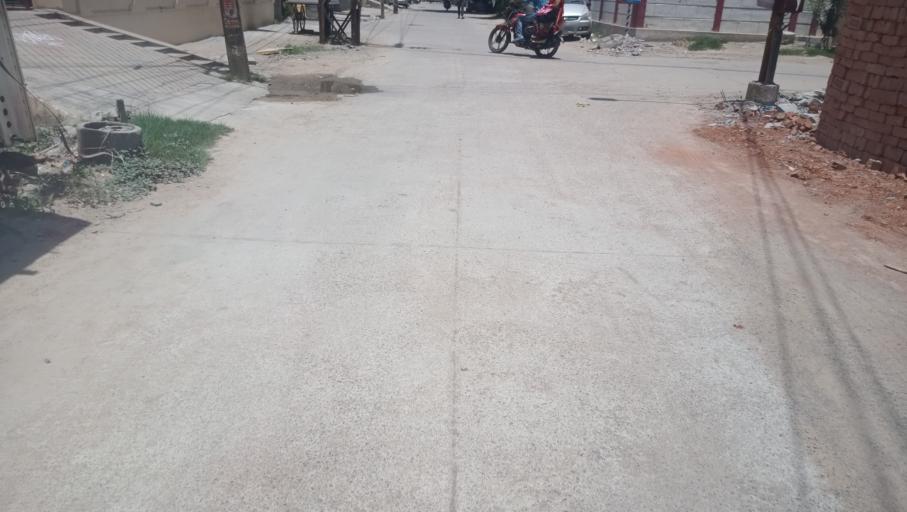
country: IN
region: Telangana
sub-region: Rangareddi
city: Uppal Kalan
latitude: 17.3984
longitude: 78.5627
